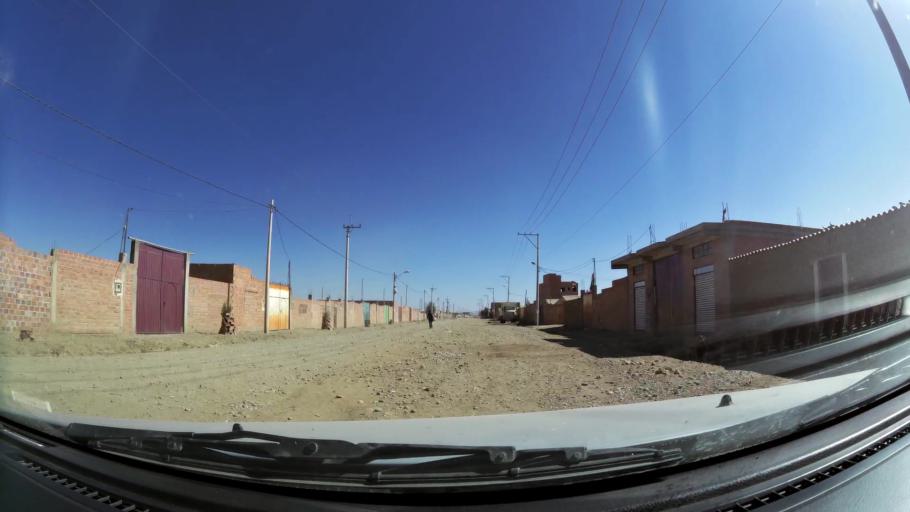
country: BO
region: La Paz
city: La Paz
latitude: -16.6040
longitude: -68.2009
